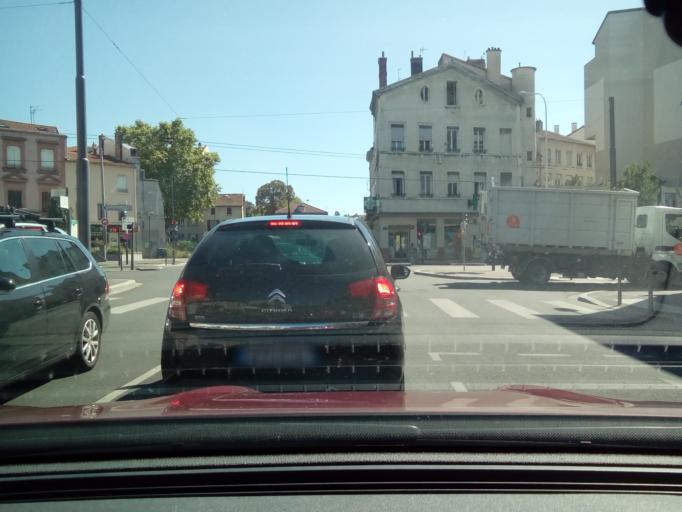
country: FR
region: Rhone-Alpes
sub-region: Departement du Rhone
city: Villeurbanne
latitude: 45.7561
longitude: 4.8762
